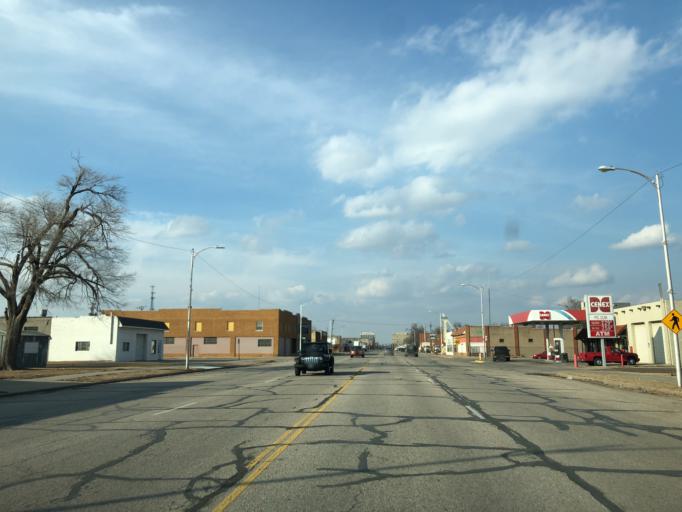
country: US
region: Kansas
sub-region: Reno County
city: South Hutchinson
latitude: 38.0410
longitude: -97.9318
